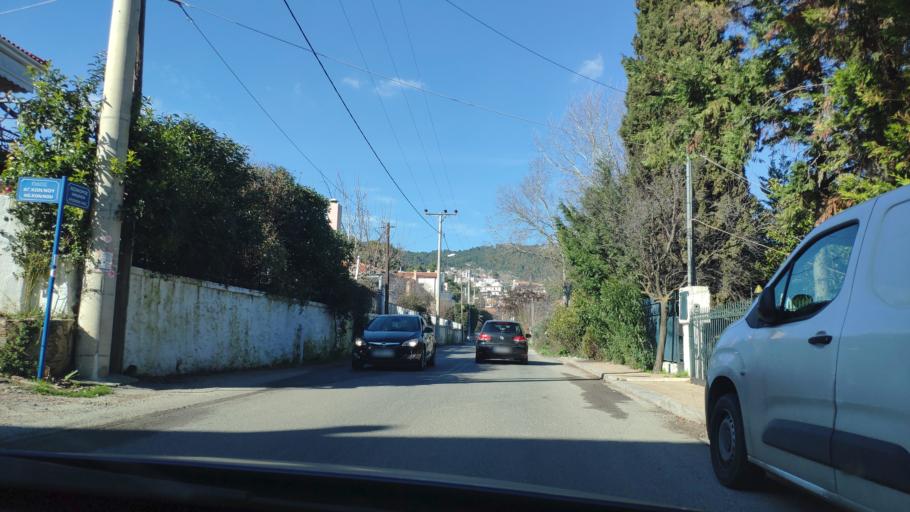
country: GR
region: Attica
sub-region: Nomarchia Anatolikis Attikis
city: Afidnes
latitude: 38.1995
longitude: 23.8409
